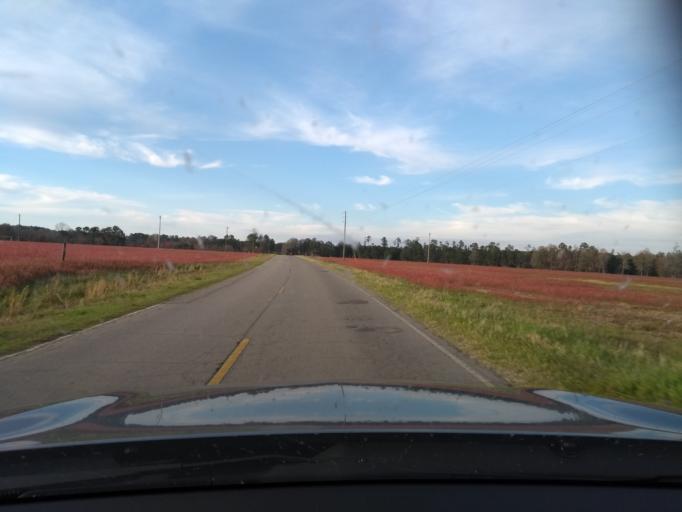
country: US
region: Georgia
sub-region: Bulloch County
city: Brooklet
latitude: 32.2812
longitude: -81.7577
